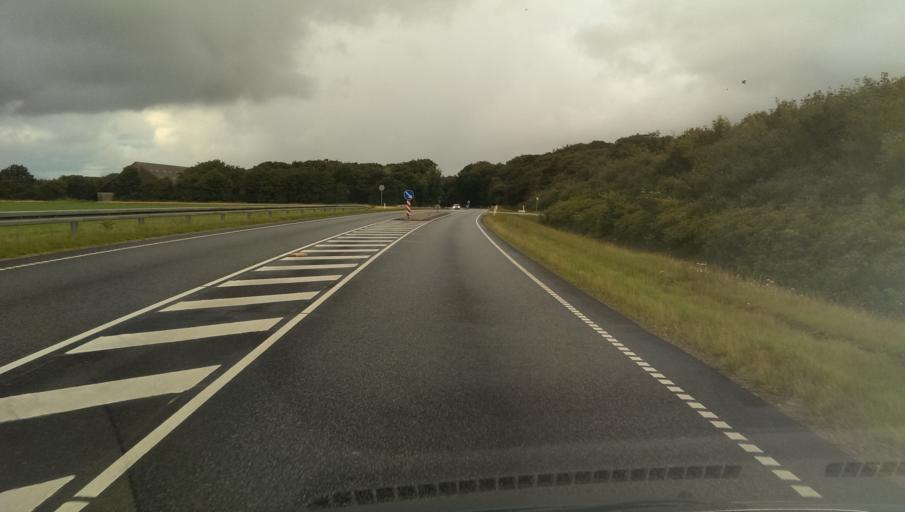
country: DK
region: South Denmark
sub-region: Varde Kommune
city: Olgod
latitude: 55.6848
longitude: 8.5924
